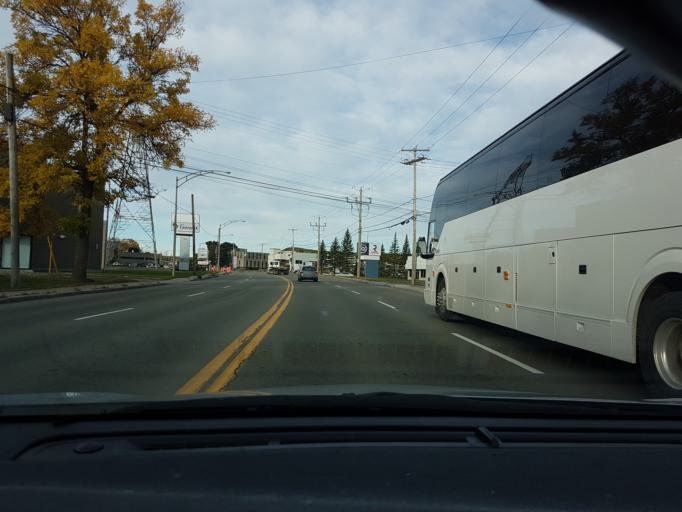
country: CA
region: Quebec
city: L'Ancienne-Lorette
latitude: 46.8061
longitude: -71.3218
